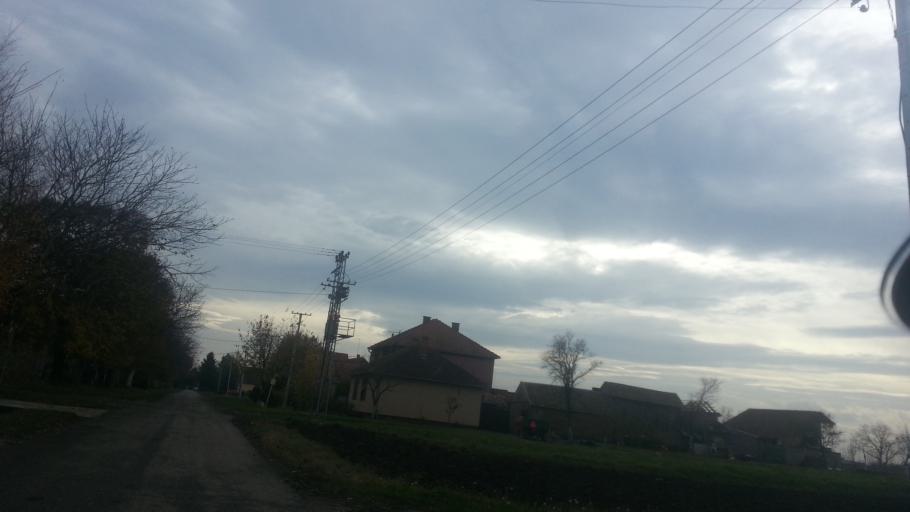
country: RS
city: Golubinci
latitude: 44.9927
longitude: 20.0579
